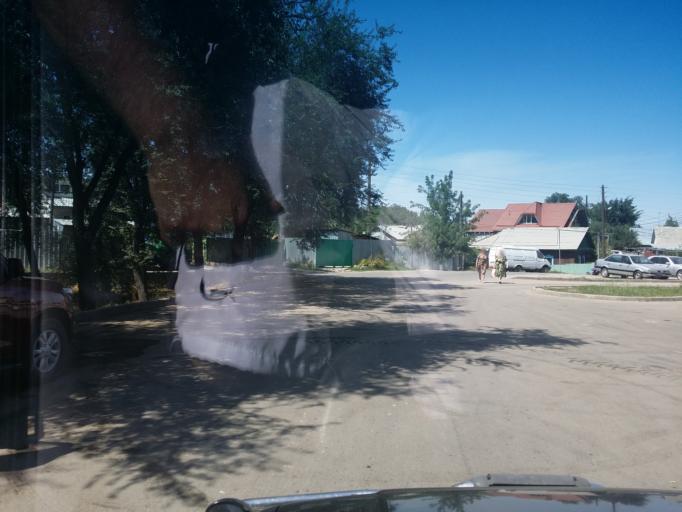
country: KZ
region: Almaty Oblysy
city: Pervomayskiy
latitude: 43.3555
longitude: 76.9473
